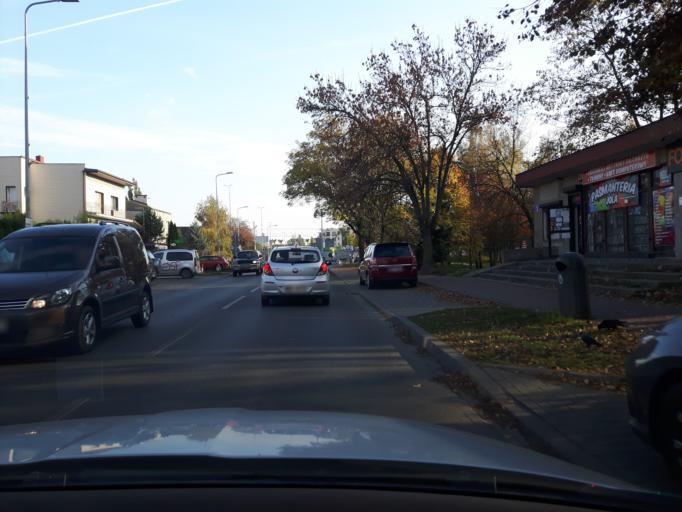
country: PL
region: Masovian Voivodeship
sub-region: Powiat wolominski
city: Zabki
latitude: 52.2946
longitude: 21.1132
